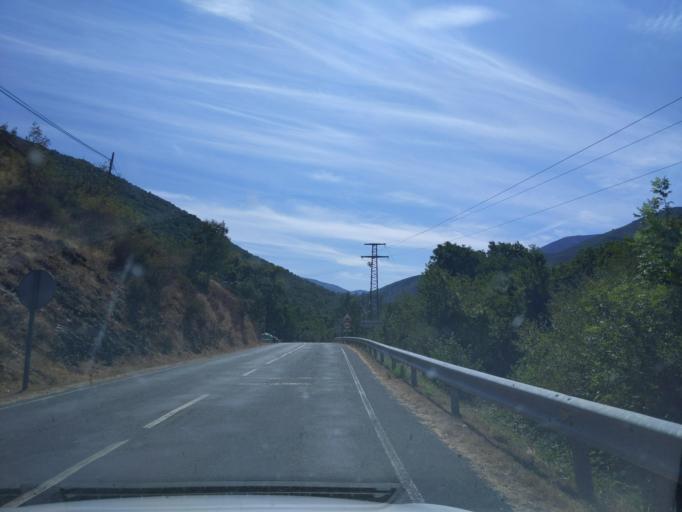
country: ES
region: La Rioja
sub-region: Provincia de La Rioja
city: Zorraquin
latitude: 42.2829
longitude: -3.0271
